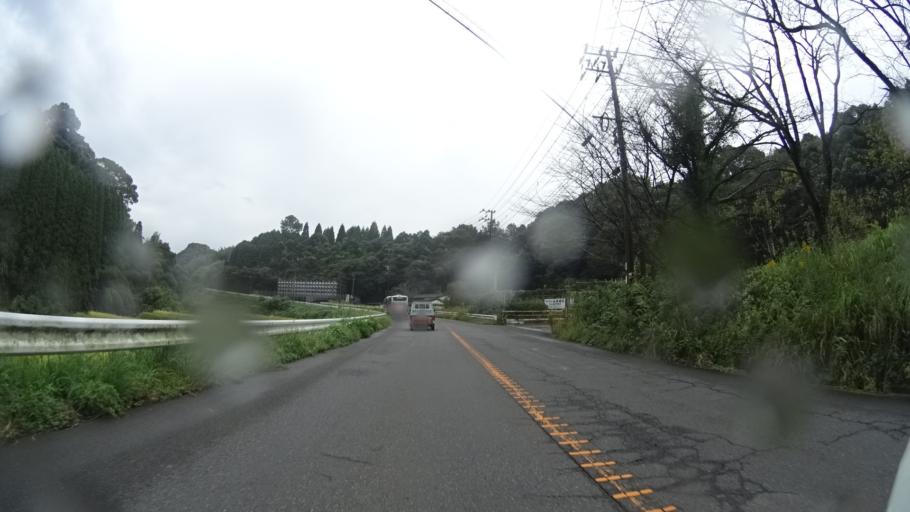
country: JP
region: Kagoshima
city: Kajiki
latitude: 31.7710
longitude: 130.6706
